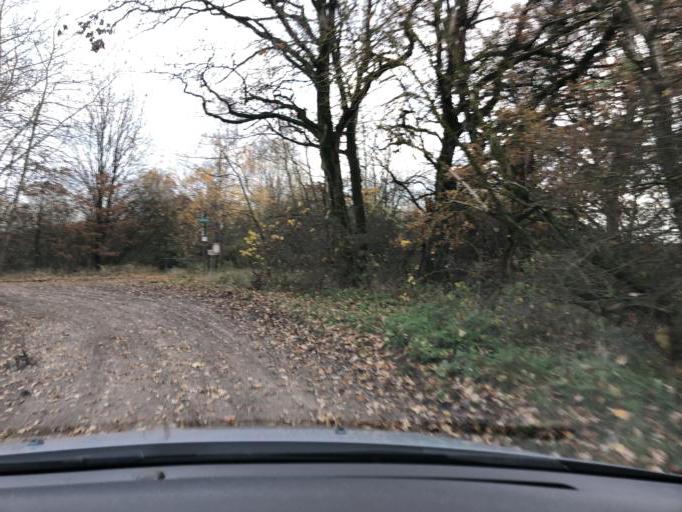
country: DE
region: Saxony
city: Mutzschen
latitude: 51.2784
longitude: 12.8991
